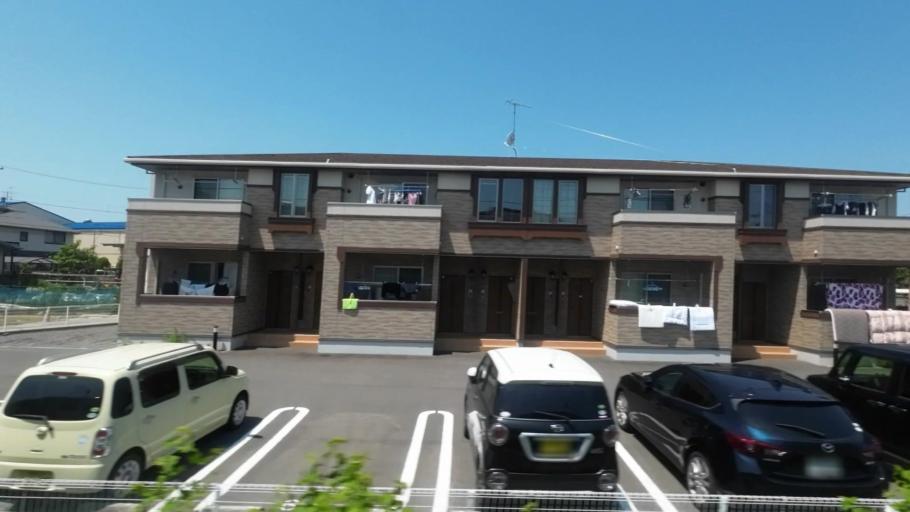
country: JP
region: Ehime
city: Hojo
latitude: 33.9636
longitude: 132.7743
